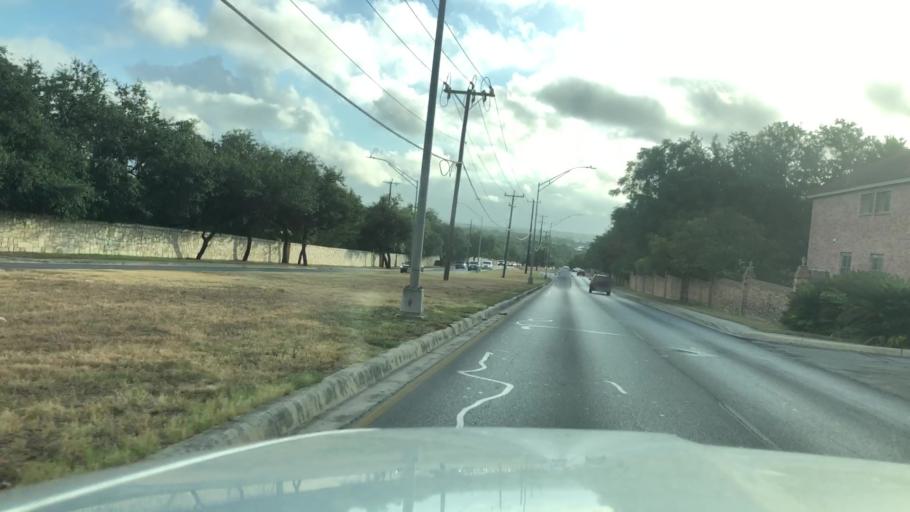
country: US
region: Texas
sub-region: Bexar County
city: Shavano Park
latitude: 29.5659
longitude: -98.5565
